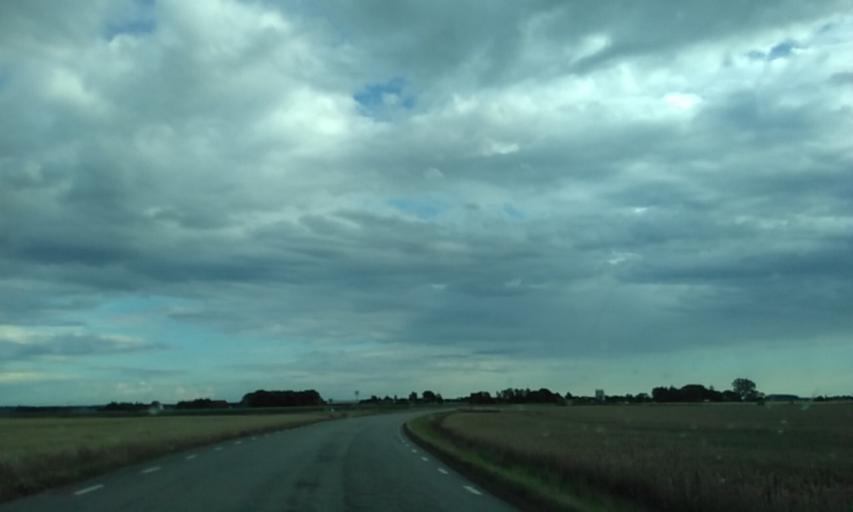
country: SE
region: Vaestra Goetaland
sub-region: Grastorps Kommun
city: Graestorp
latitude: 58.4202
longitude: 12.7261
